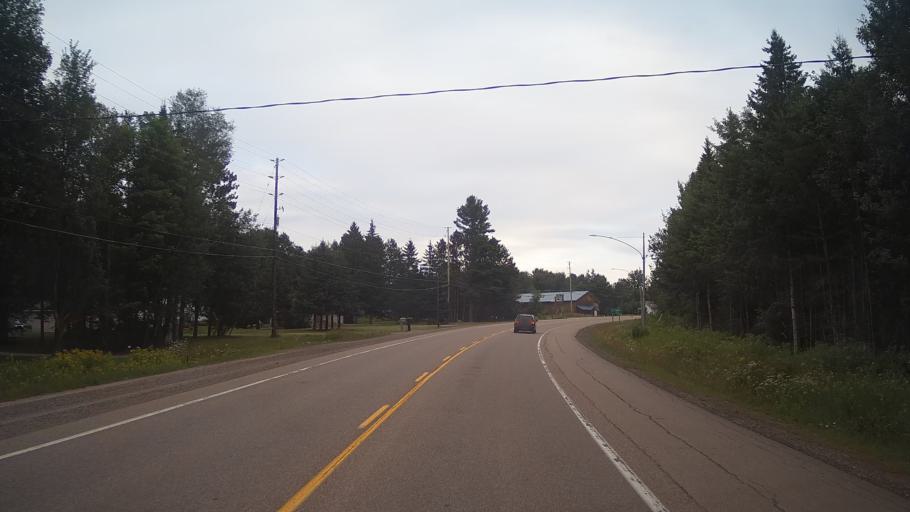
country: CA
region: Ontario
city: Deep River
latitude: 46.0781
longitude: -77.4782
